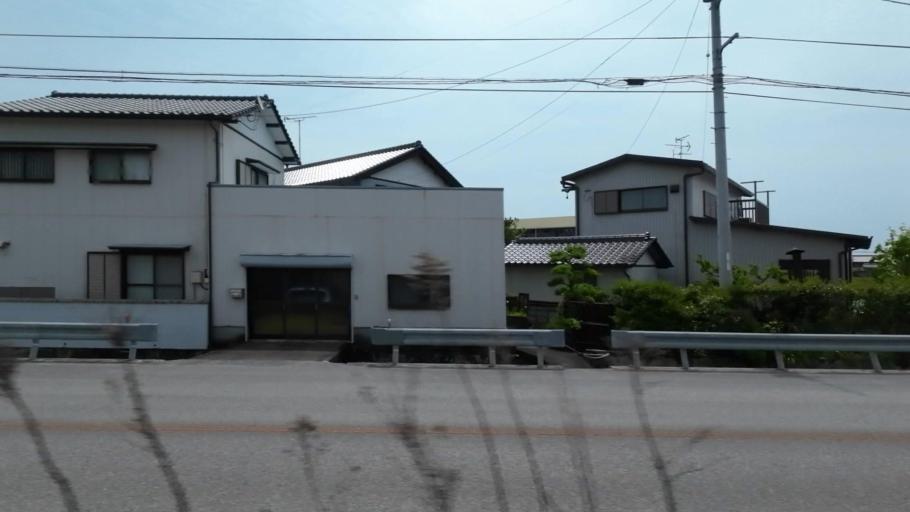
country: JP
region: Kochi
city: Kochi-shi
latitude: 33.5880
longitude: 133.6579
